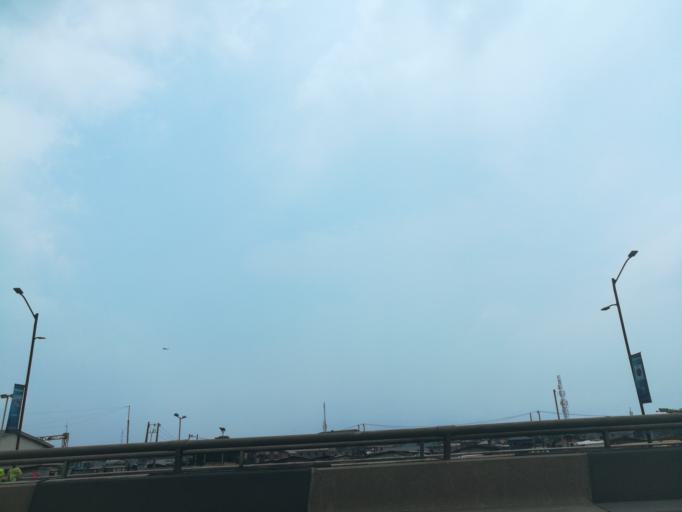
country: NG
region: Lagos
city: Somolu
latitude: 6.5447
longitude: 3.3984
